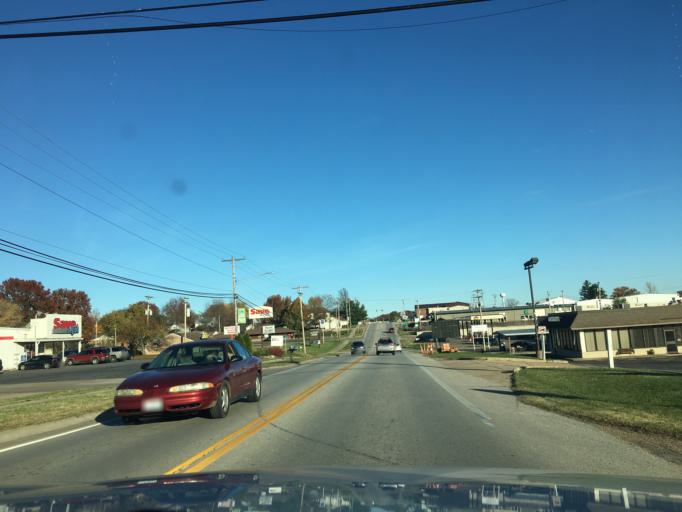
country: US
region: Missouri
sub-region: Franklin County
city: New Haven
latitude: 38.6006
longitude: -91.2244
